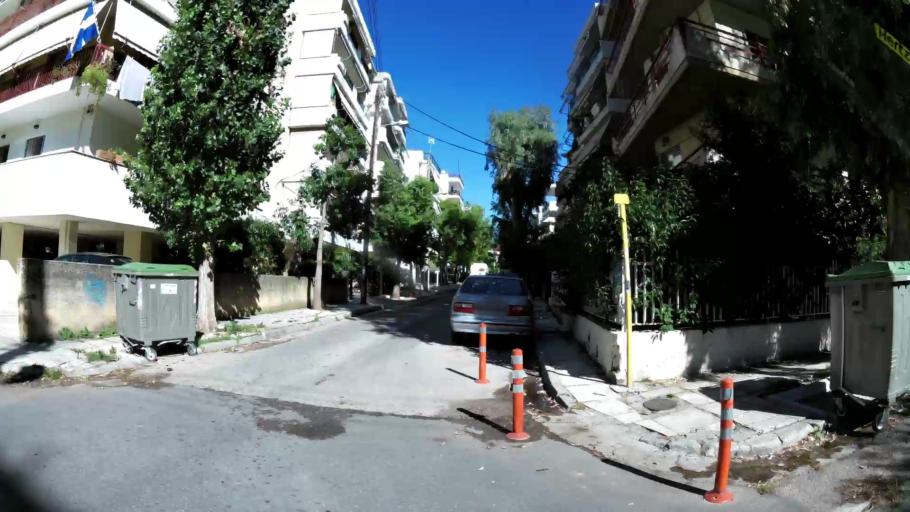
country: GR
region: Attica
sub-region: Nomarchia Athinas
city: Khalandrion
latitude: 38.0291
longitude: 23.8028
